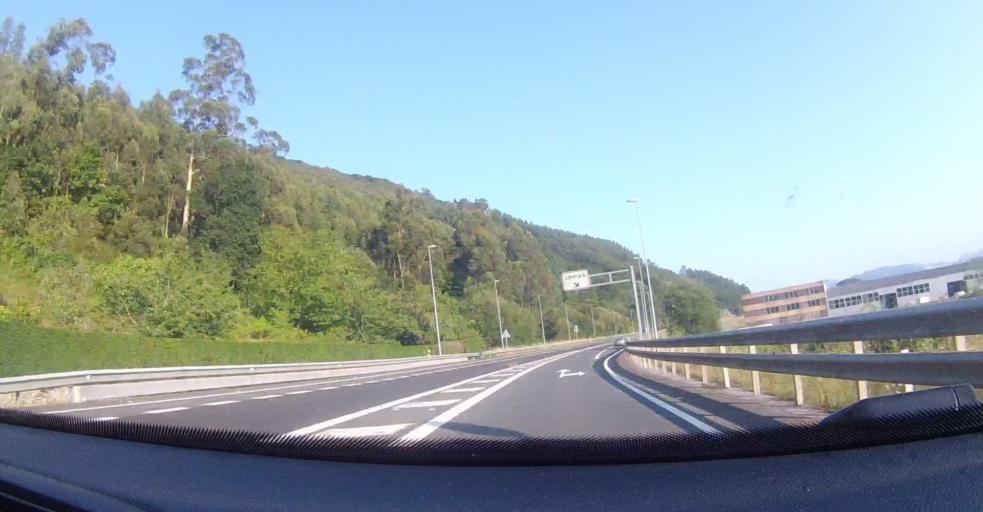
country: ES
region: Cantabria
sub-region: Provincia de Cantabria
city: Limpias
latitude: 43.3767
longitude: -3.4308
